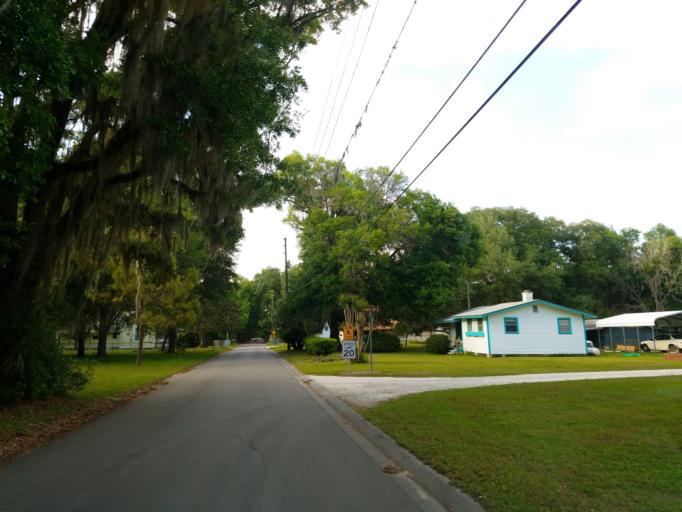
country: US
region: Florida
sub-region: Alachua County
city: Gainesville
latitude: 29.5058
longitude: -82.2816
